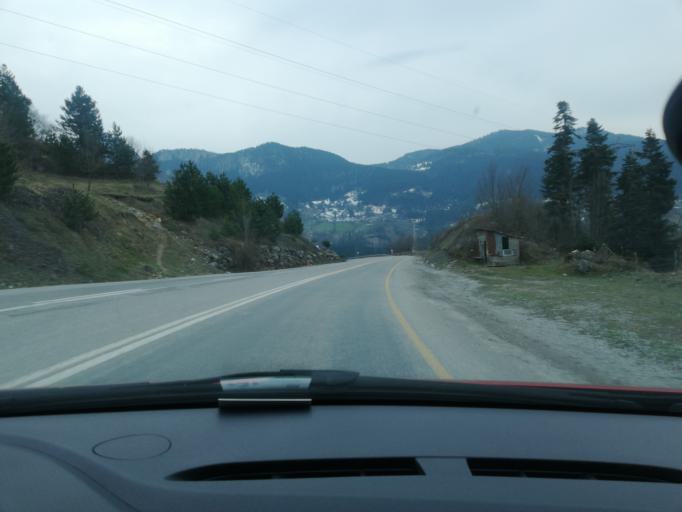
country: TR
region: Kastamonu
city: Kure
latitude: 41.8488
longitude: 33.7207
